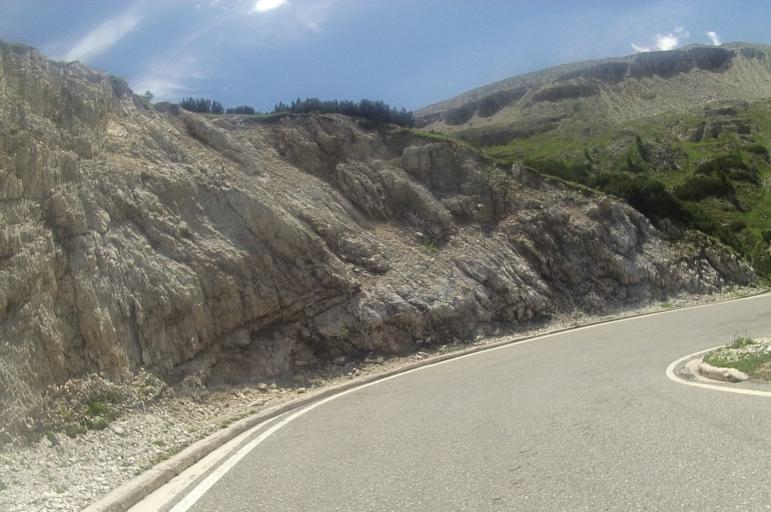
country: IT
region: Trentino-Alto Adige
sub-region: Bolzano
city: Sesto
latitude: 46.6069
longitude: 12.2945
